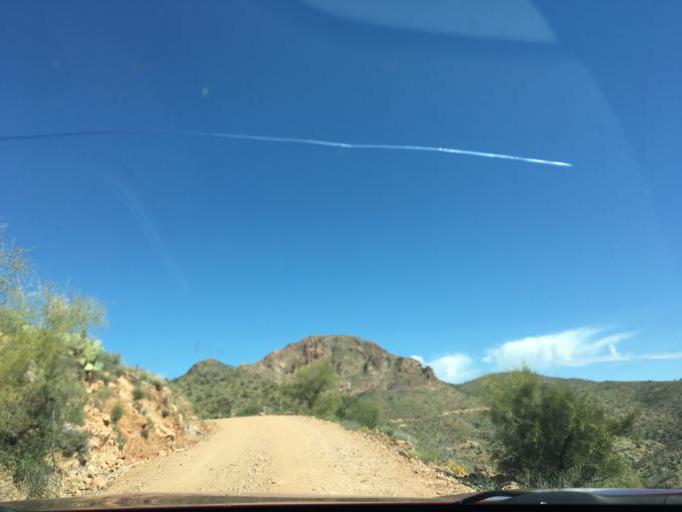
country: US
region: Arizona
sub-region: Yavapai County
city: Bagdad
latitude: 34.6091
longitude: -113.3999
